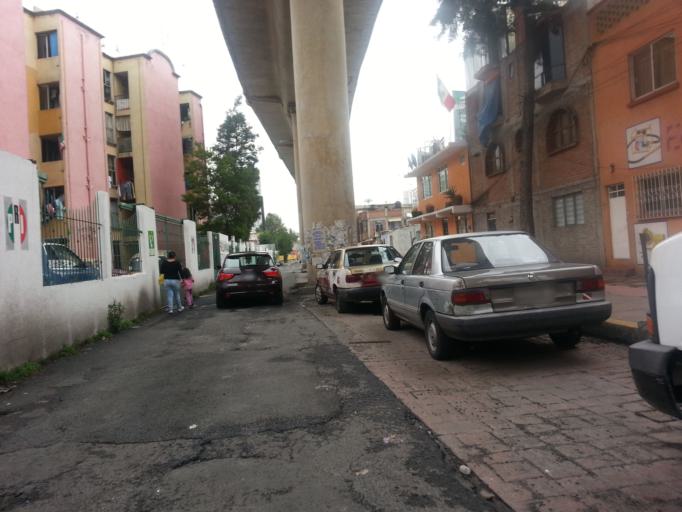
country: MX
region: Mexico City
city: Alvaro Obregon
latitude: 19.3817
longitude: -99.1933
